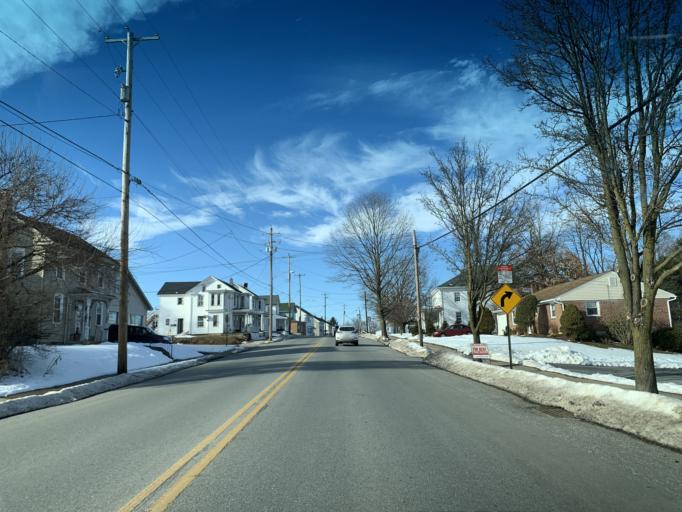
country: US
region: Pennsylvania
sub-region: York County
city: Dillsburg
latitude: 40.1041
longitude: -77.0332
